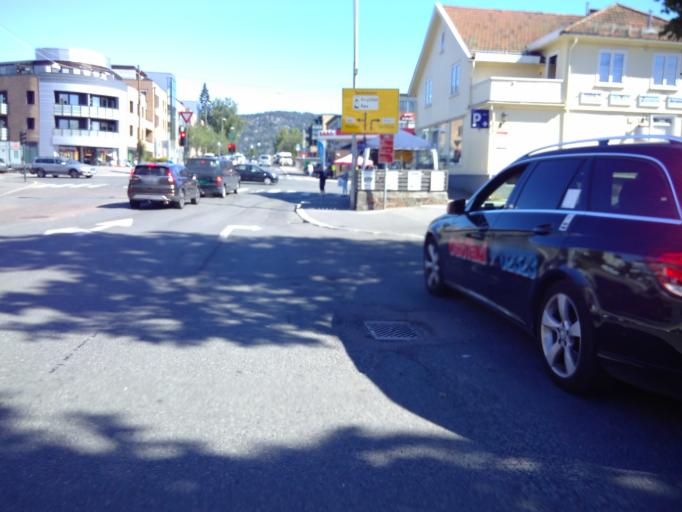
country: NO
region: Akershus
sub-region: Baerum
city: Lysaker
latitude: 59.9472
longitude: 10.6430
